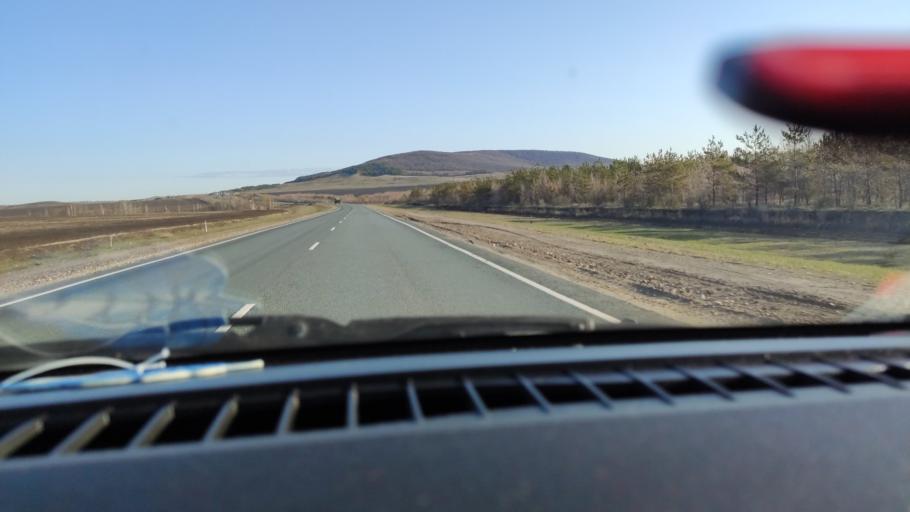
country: RU
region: Saratov
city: Alekseyevka
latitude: 52.2784
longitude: 47.9316
